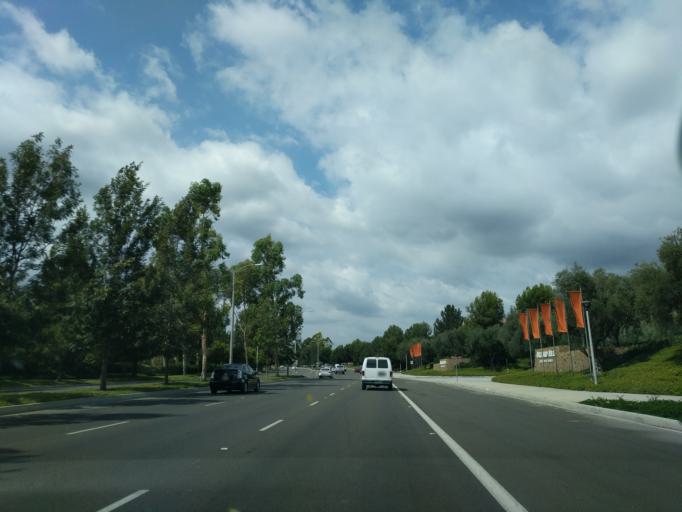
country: US
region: California
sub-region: Orange County
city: North Tustin
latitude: 33.7370
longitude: -117.7642
